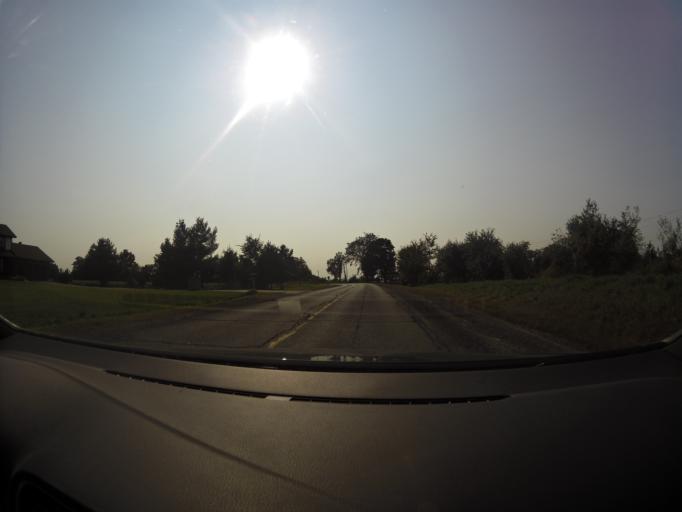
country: CA
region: Ontario
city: Bells Corners
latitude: 45.3416
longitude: -76.0467
